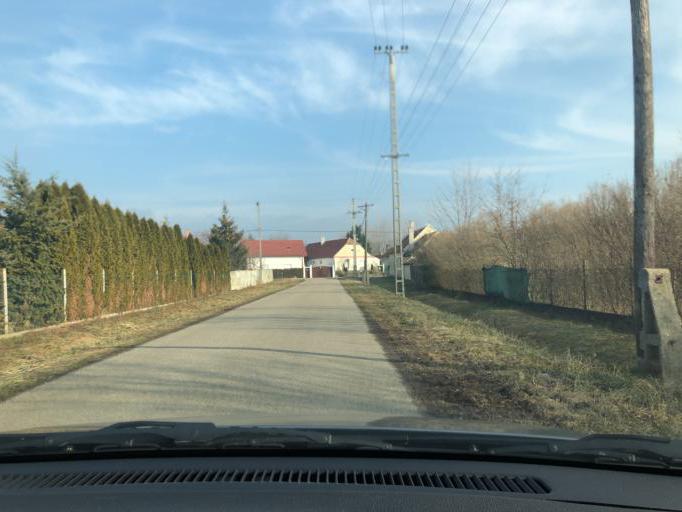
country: HU
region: Gyor-Moson-Sopron
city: Kapuvar
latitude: 47.6031
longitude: 17.0820
